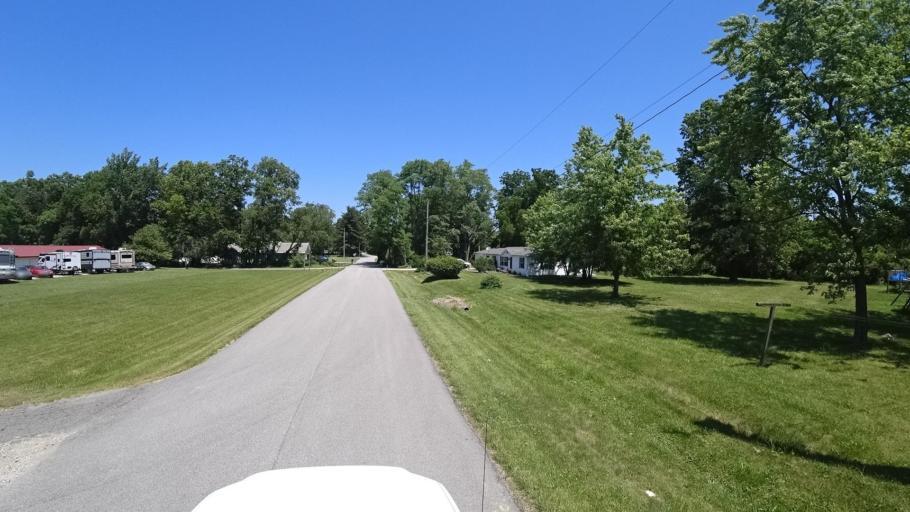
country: US
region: Indiana
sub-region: Porter County
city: Burns Harbor
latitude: 41.6033
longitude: -87.1259
